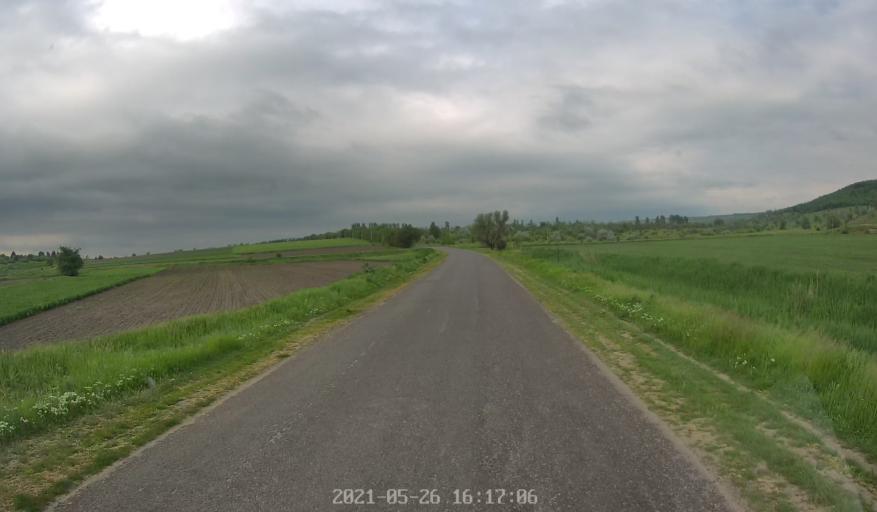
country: MD
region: Hincesti
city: Dancu
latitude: 46.7289
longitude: 28.3596
